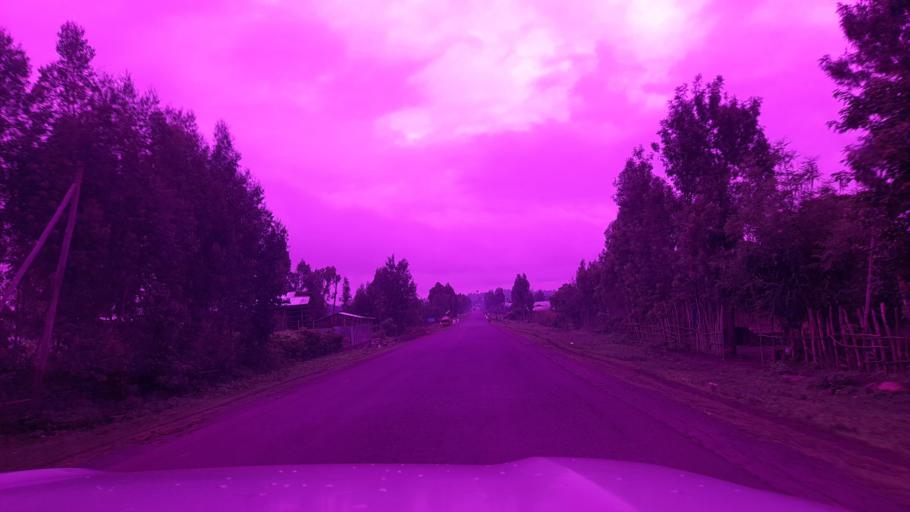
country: ET
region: Oromiya
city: Waliso
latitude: 8.2802
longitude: 37.6927
